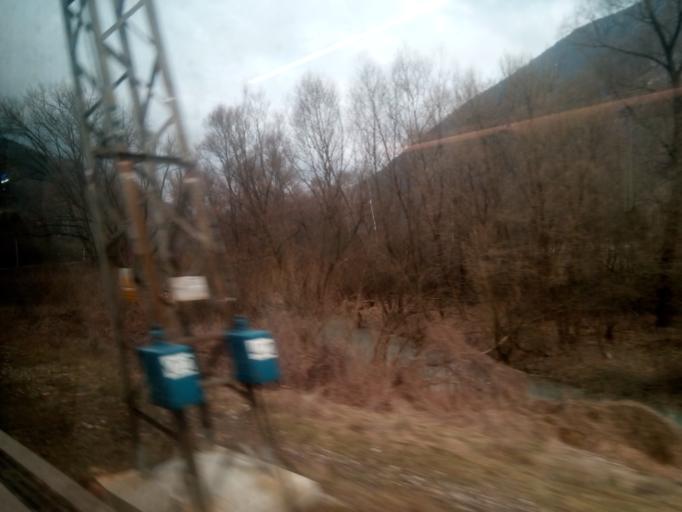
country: SK
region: Zilinsky
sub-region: Okres Zilina
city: Vrutky
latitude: 49.1348
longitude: 18.8940
